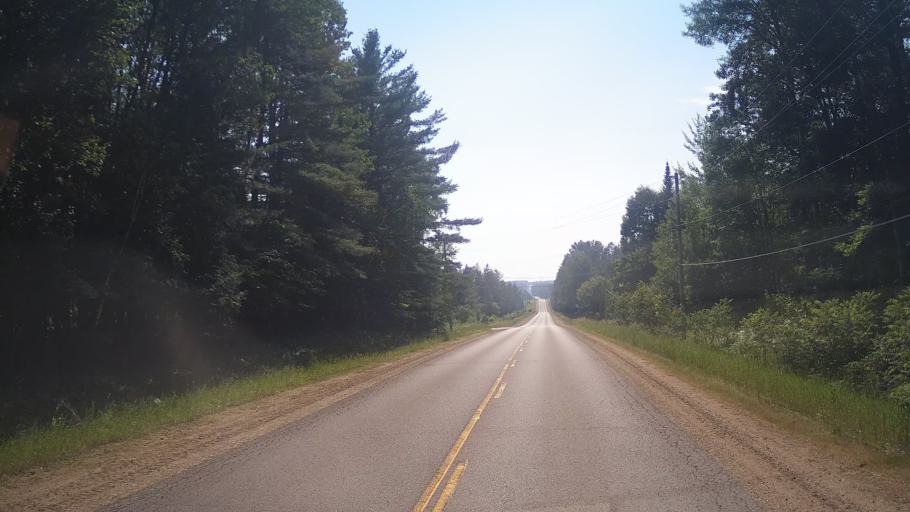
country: CA
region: Ontario
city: Pembroke
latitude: 45.6153
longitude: -77.1845
